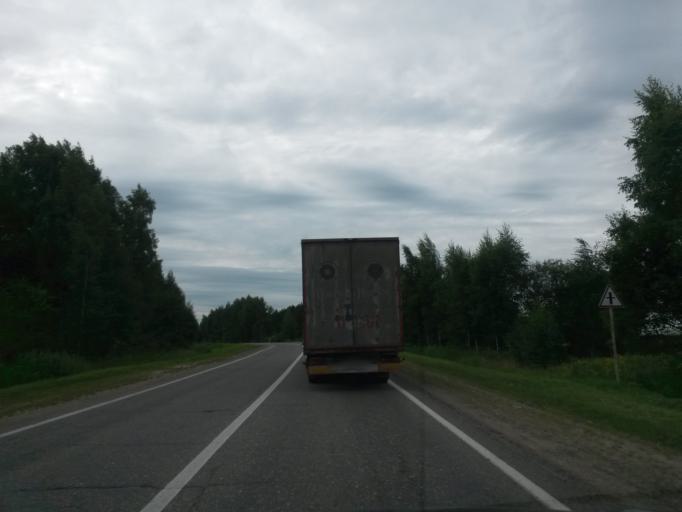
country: RU
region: Jaroslavl
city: Krasnyye Tkachi
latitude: 57.3668
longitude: 39.7373
